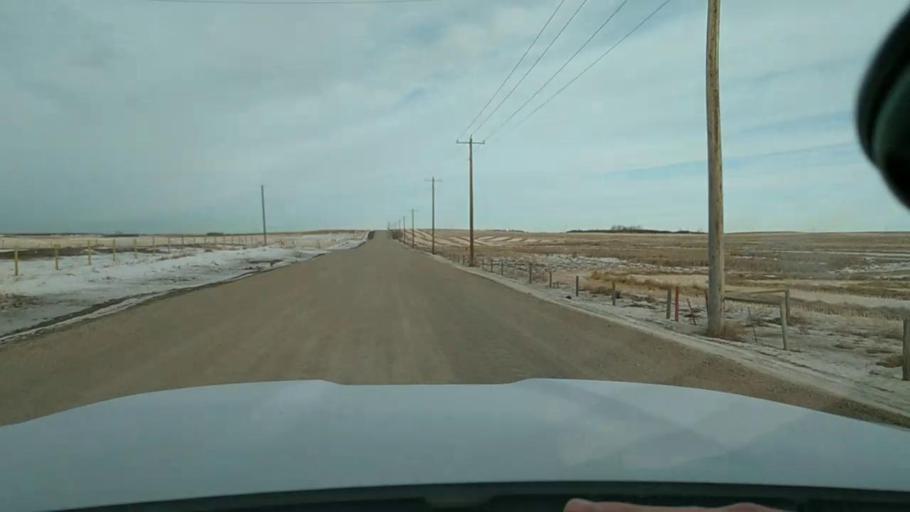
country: CA
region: Alberta
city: Airdrie
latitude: 51.2333
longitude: -113.9118
